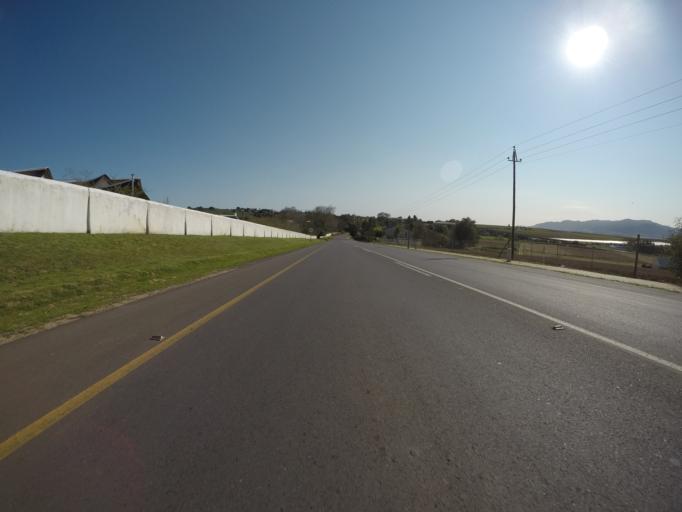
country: ZA
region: Western Cape
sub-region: Cape Winelands District Municipality
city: Noorder-Paarl
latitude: -33.6708
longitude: 18.9214
